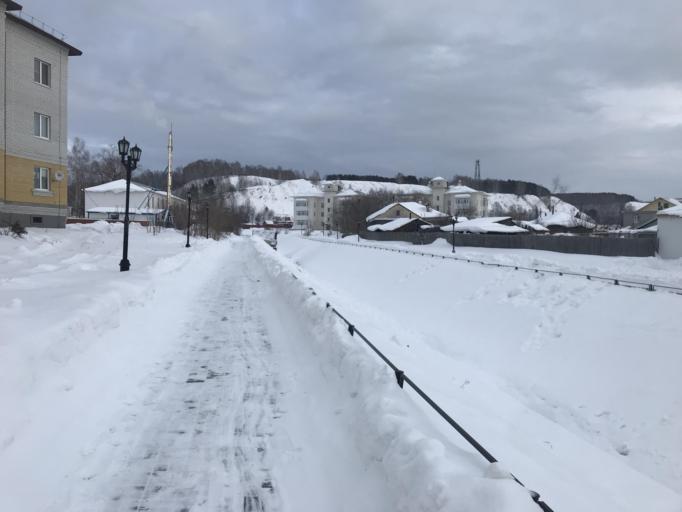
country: RU
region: Tjumen
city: Tobol'sk
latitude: 58.1954
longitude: 68.2502
